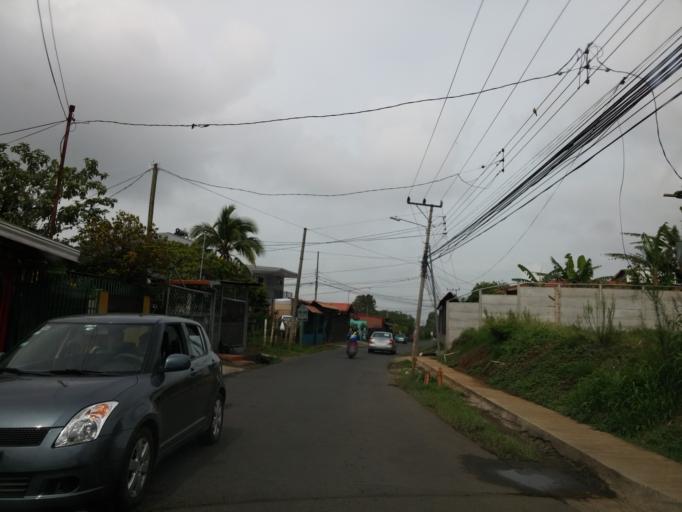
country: CR
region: Heredia
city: Llorente
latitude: 10.0186
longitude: -84.1637
